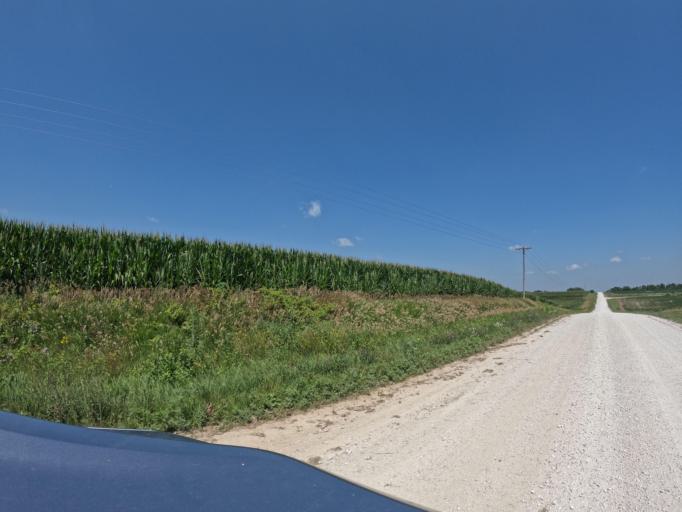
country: US
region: Iowa
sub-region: Keokuk County
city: Sigourney
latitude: 41.2771
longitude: -92.2381
